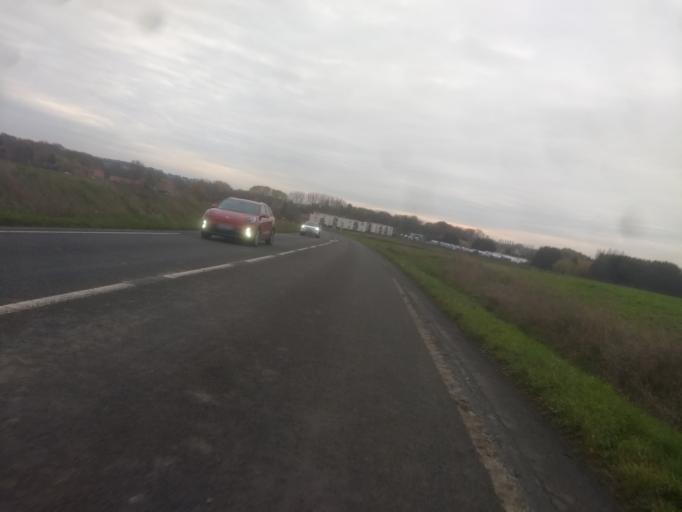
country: FR
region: Nord-Pas-de-Calais
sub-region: Departement du Pas-de-Calais
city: Achicourt
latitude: 50.2696
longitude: 2.7475
